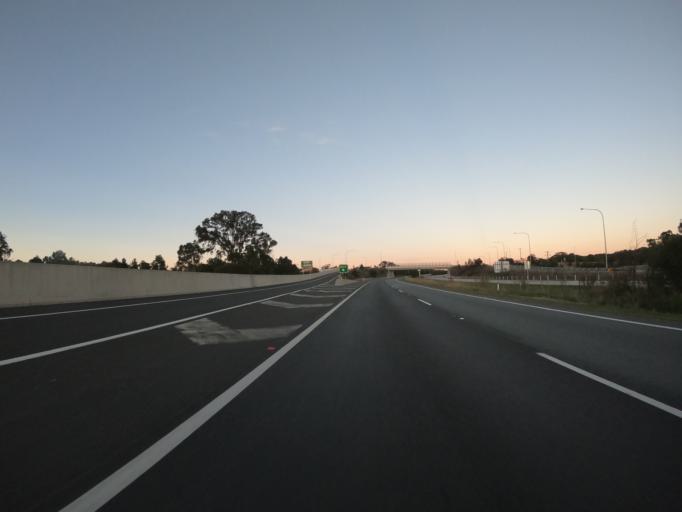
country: AU
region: New South Wales
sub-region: Goulburn Mulwaree
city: Goulburn
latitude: -34.7293
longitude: 149.9836
